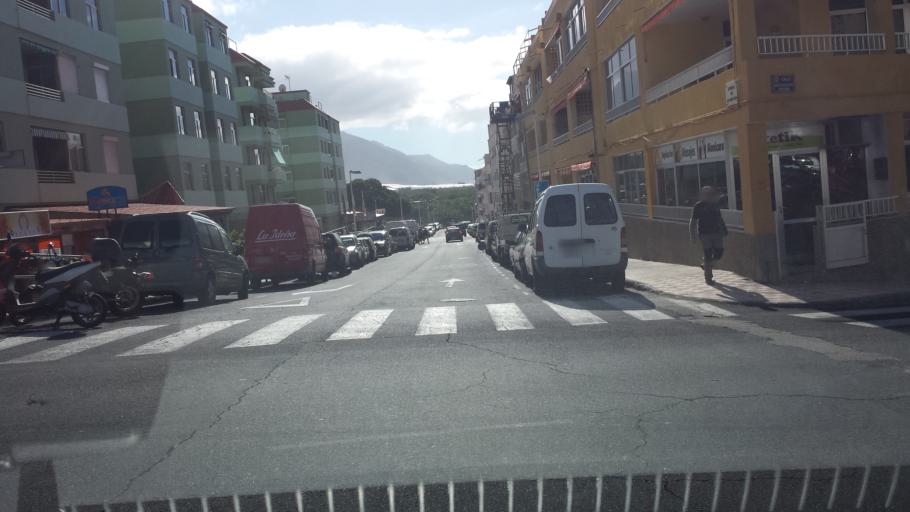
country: ES
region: Canary Islands
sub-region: Provincia de Santa Cruz de Tenerife
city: Tazacorte
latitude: 28.5877
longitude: -17.9098
